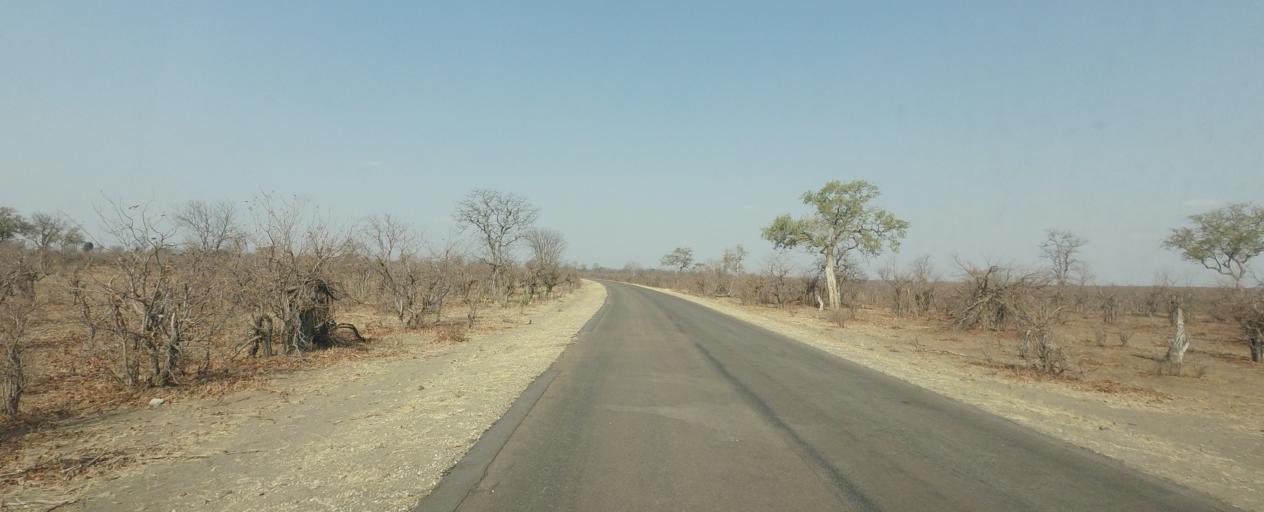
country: ZA
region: Limpopo
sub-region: Mopani District Municipality
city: Giyani
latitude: -23.0978
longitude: 31.4079
